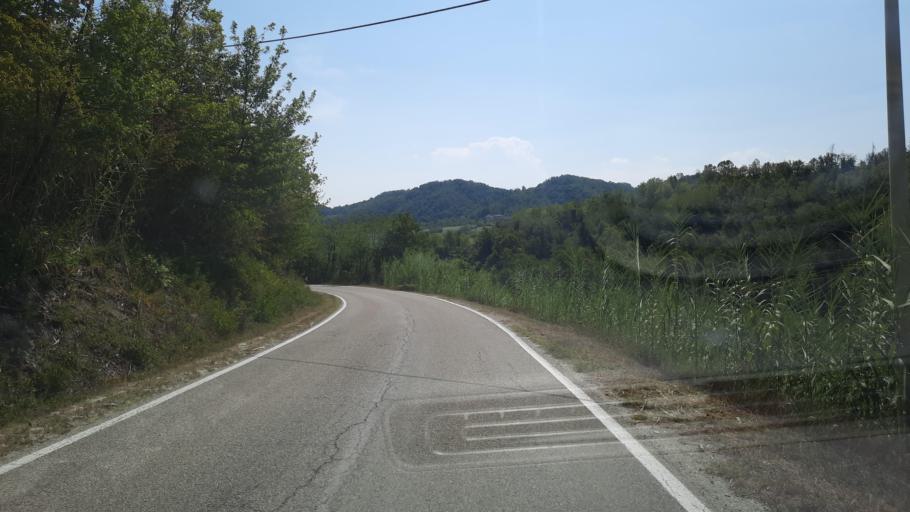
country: IT
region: Piedmont
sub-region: Provincia di Alessandria
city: Mombello Monferrato
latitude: 45.1567
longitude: 8.2525
